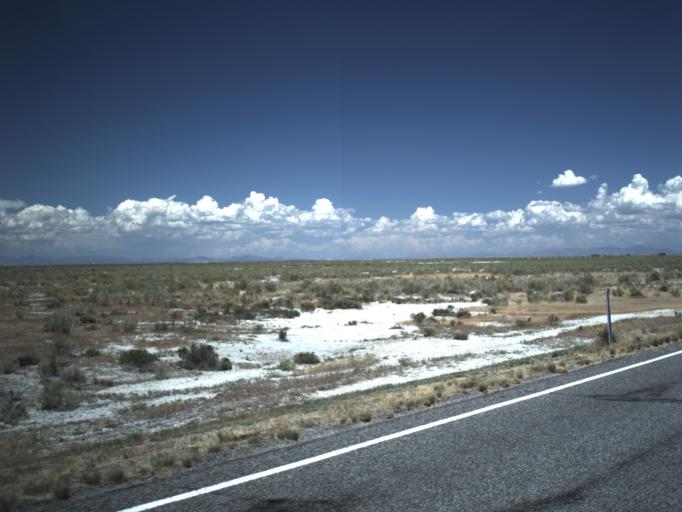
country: US
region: Utah
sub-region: Millard County
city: Delta
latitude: 39.3105
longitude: -112.7746
